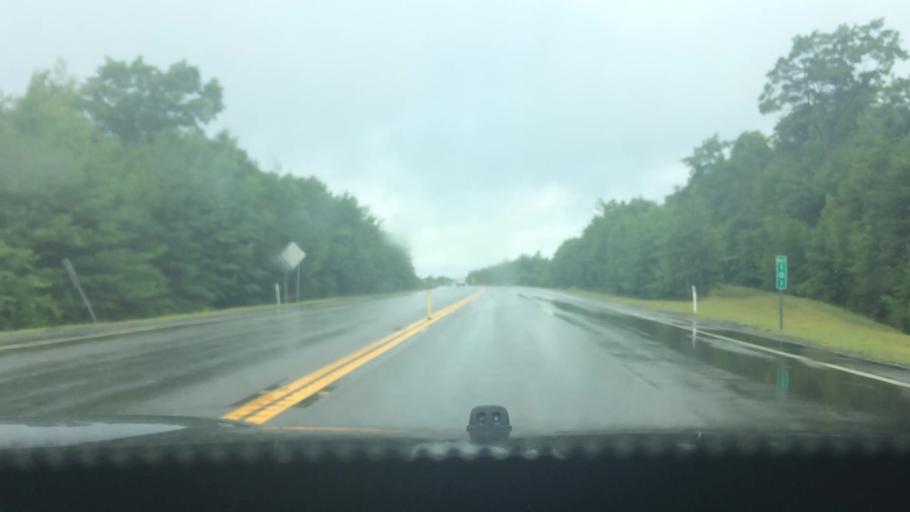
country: US
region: Massachusetts
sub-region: Worcester County
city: South Ashburnham
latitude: 42.5944
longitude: -71.9639
